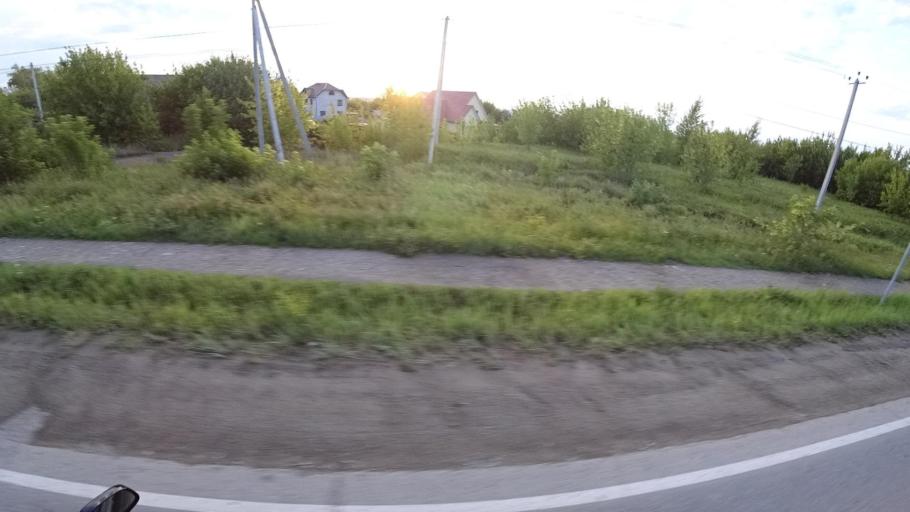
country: RU
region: Sverdlovsk
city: Kamyshlov
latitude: 56.8549
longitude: 62.7193
